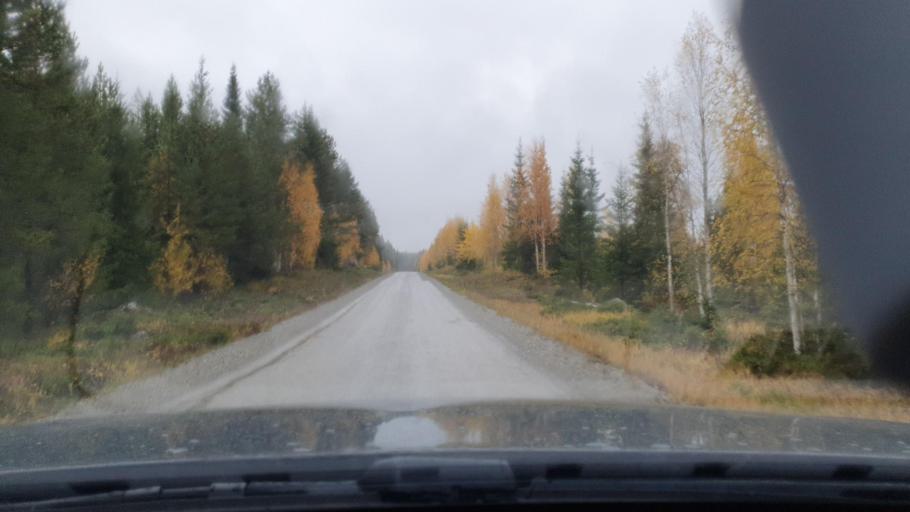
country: SE
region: Jaemtland
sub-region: Stroemsunds Kommun
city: Stroemsund
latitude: 63.5385
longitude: 15.5950
